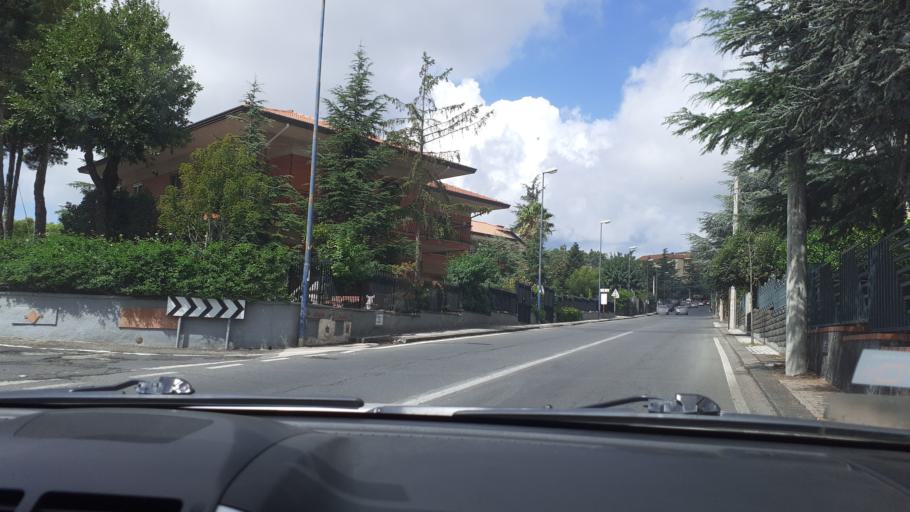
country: IT
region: Sicily
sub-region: Catania
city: Pedara
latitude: 37.6135
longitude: 15.0547
